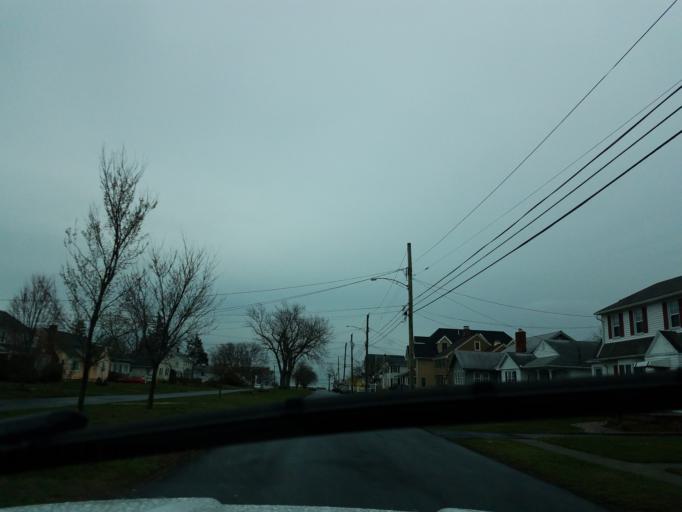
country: US
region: Connecticut
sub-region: Fairfield County
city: Stratford
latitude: 41.1512
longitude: -73.1287
